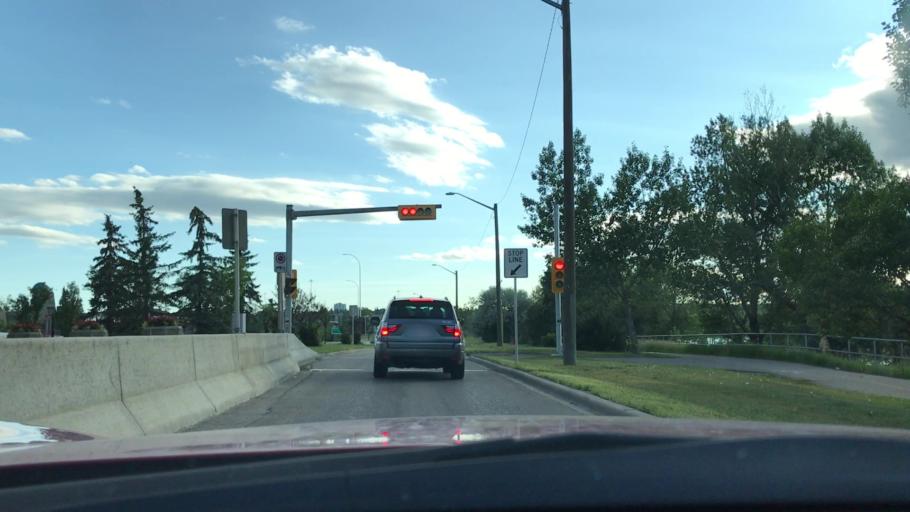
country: CA
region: Alberta
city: Calgary
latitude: 51.0489
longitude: -114.0882
